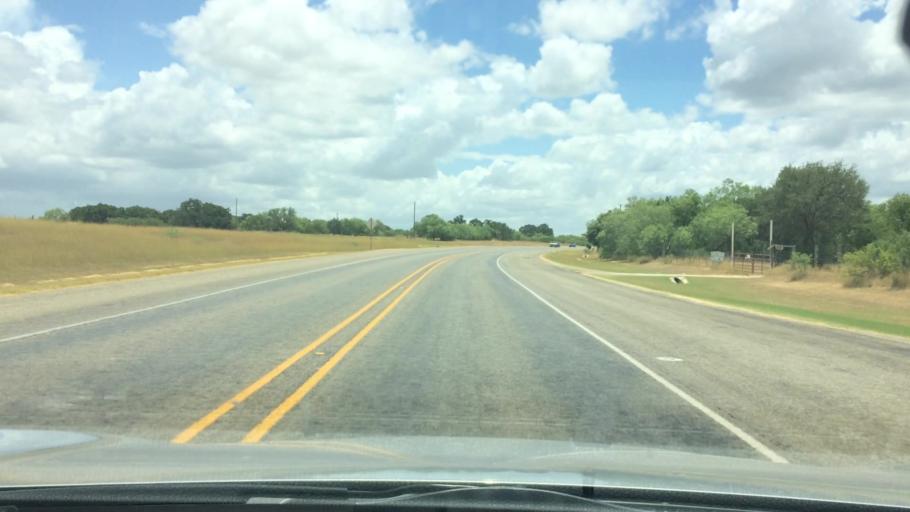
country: US
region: Texas
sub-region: Bexar County
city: Saint Hedwig
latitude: 29.3771
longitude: -98.2407
